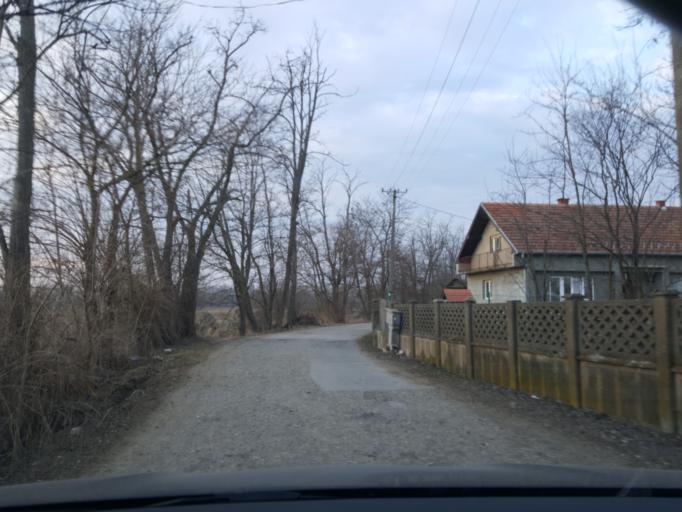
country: RS
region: Central Serbia
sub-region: Nisavski Okrug
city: Aleksinac
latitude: 43.5663
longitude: 21.6436
